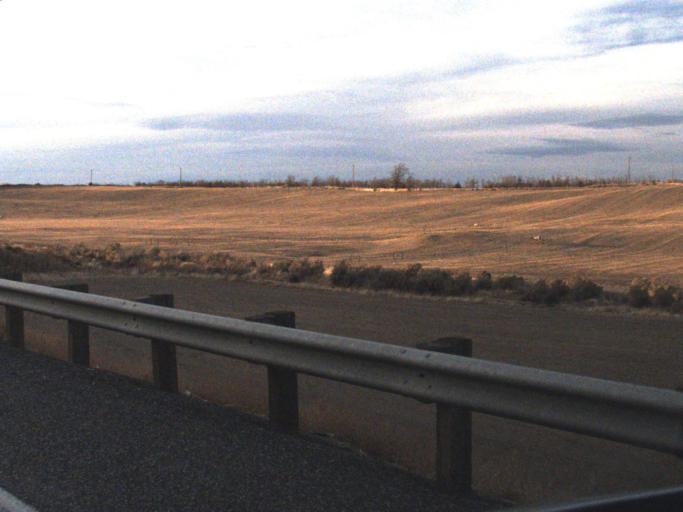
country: US
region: Washington
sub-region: Benton County
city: Finley
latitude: 46.0661
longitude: -118.8306
